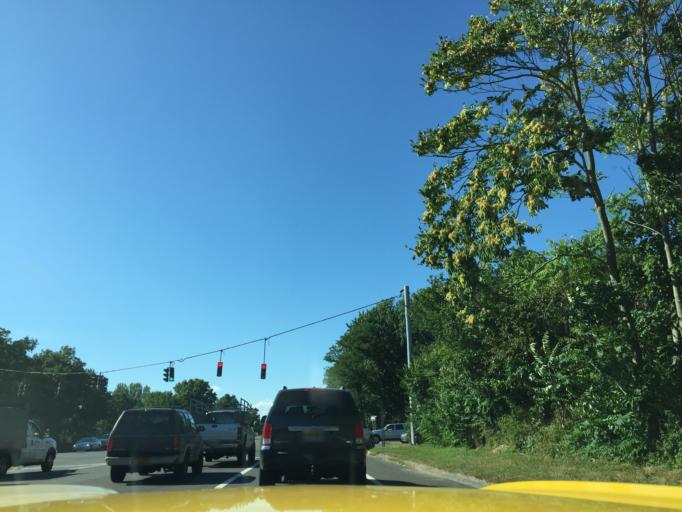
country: US
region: New York
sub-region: Suffolk County
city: Aquebogue
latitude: 40.9392
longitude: -72.6414
